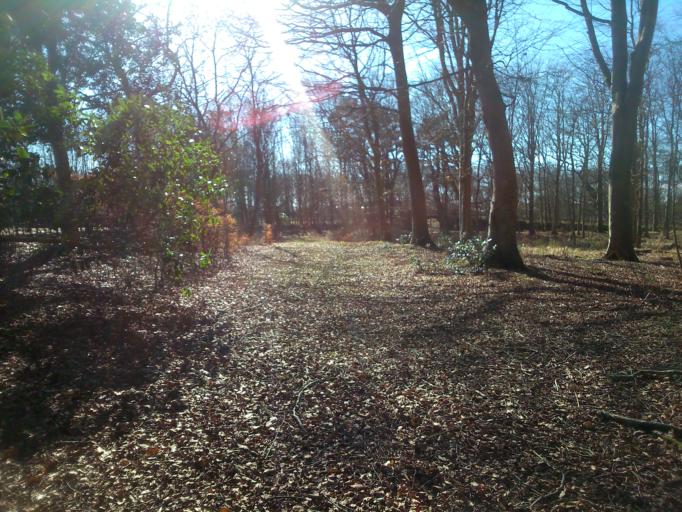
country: DK
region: Central Jutland
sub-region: Ringkobing-Skjern Kommune
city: Ringkobing
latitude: 56.0860
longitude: 8.2624
